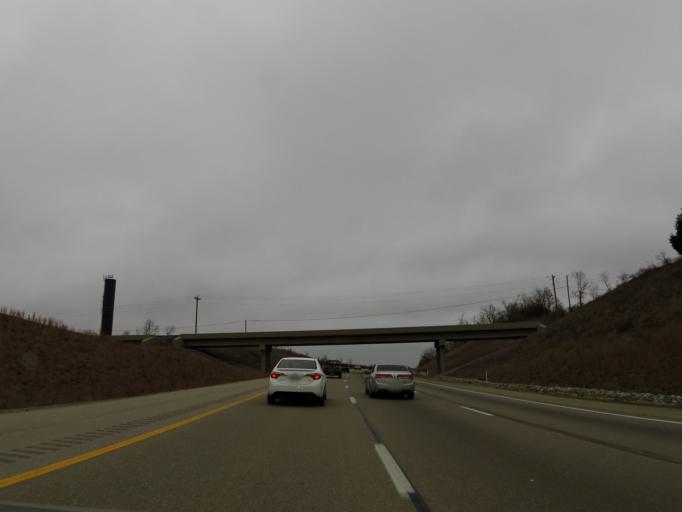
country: US
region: Kentucky
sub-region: Grant County
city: Williamstown
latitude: 38.5270
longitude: -84.5874
